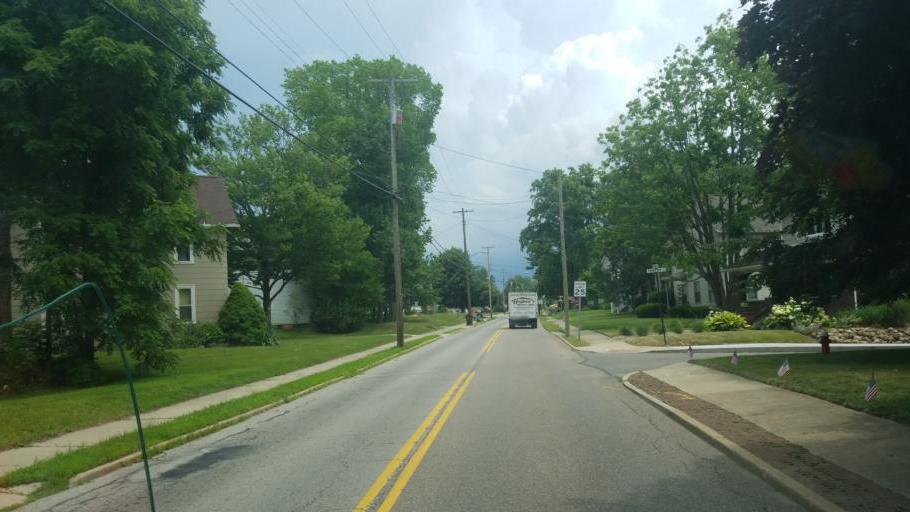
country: US
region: Ohio
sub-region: Stark County
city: North Canton
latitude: 40.8798
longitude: -81.4095
